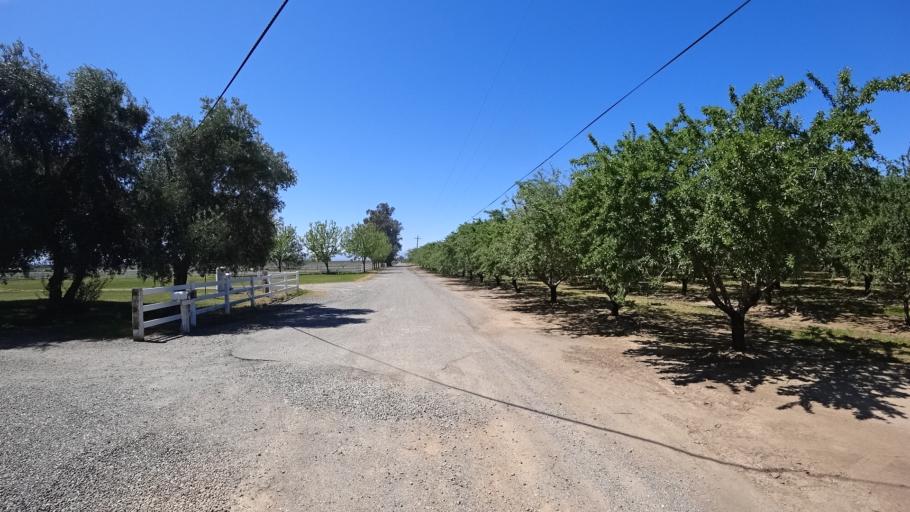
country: US
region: California
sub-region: Glenn County
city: Hamilton City
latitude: 39.7324
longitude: -122.0910
